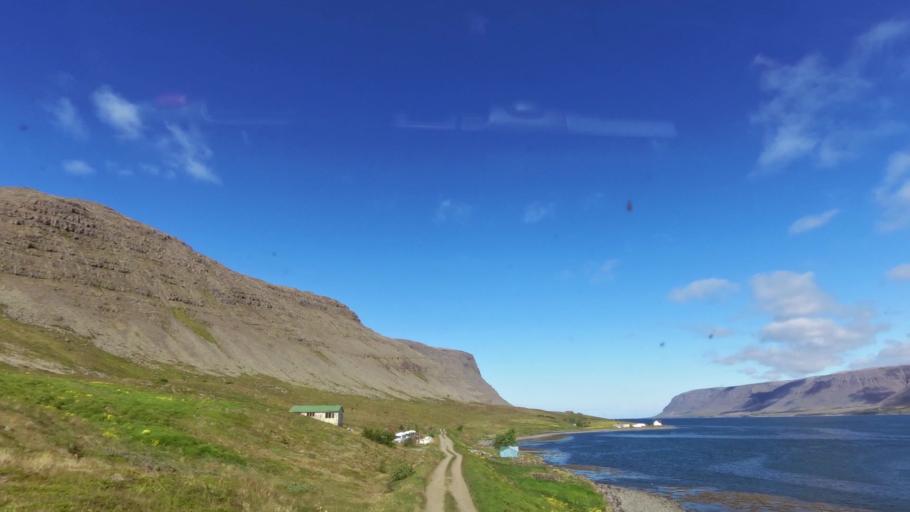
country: IS
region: West
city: Olafsvik
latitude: 65.6175
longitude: -23.8583
